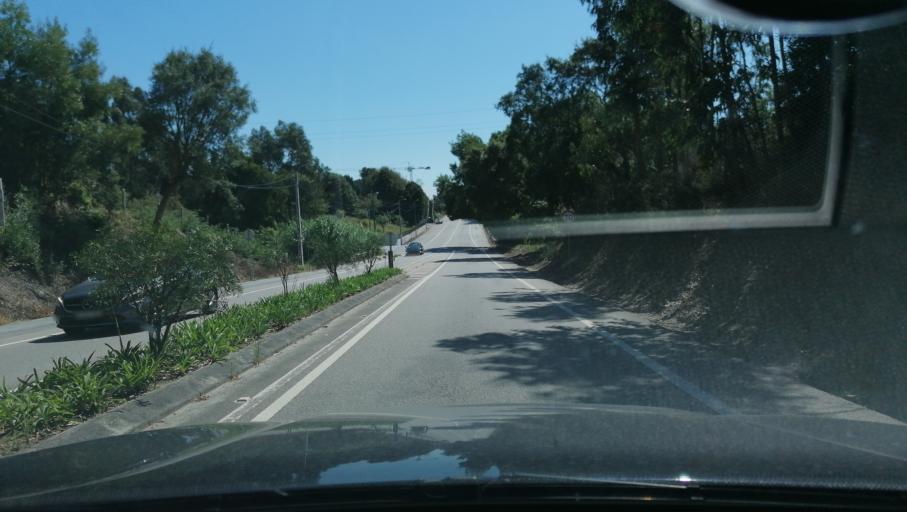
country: PT
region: Porto
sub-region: Vila Nova de Gaia
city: Gulpilhares
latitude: 41.0824
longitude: -8.6350
